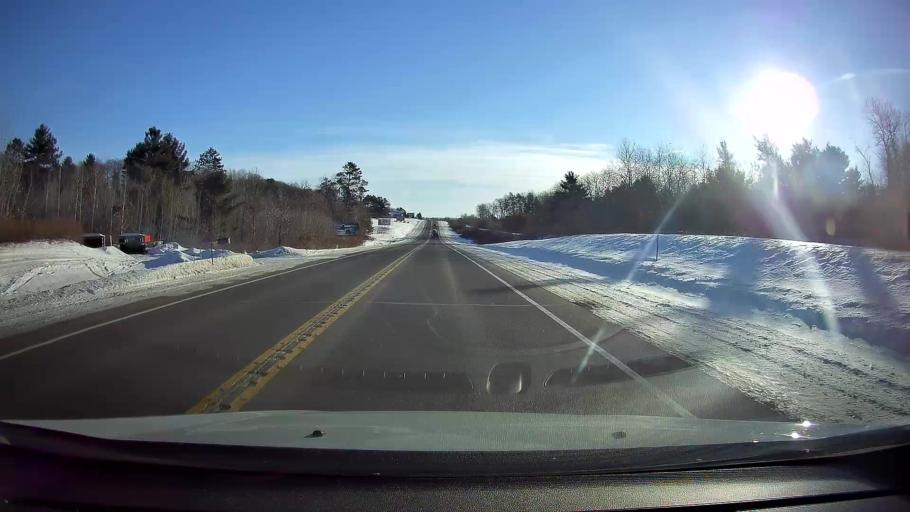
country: US
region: Wisconsin
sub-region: Sawyer County
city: Hayward
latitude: 45.9834
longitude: -91.5716
